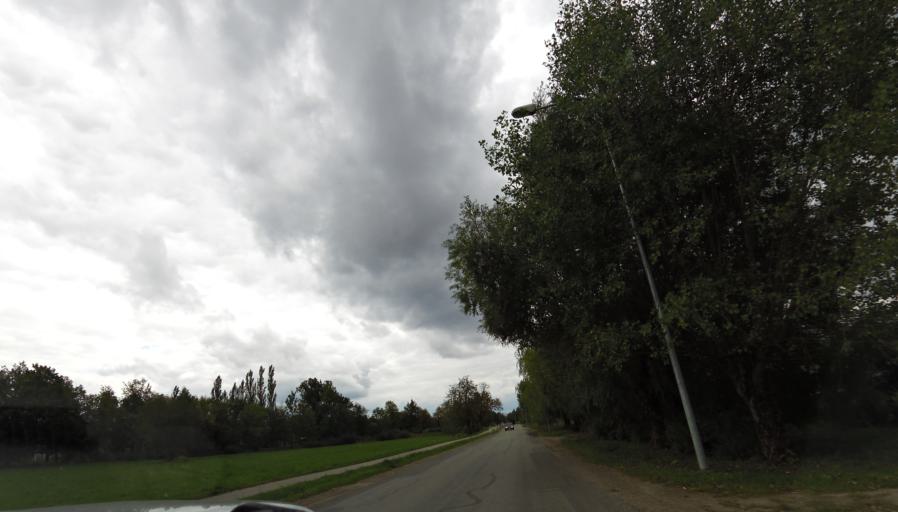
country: LT
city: Linkuva
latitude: 56.0303
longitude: 24.1659
